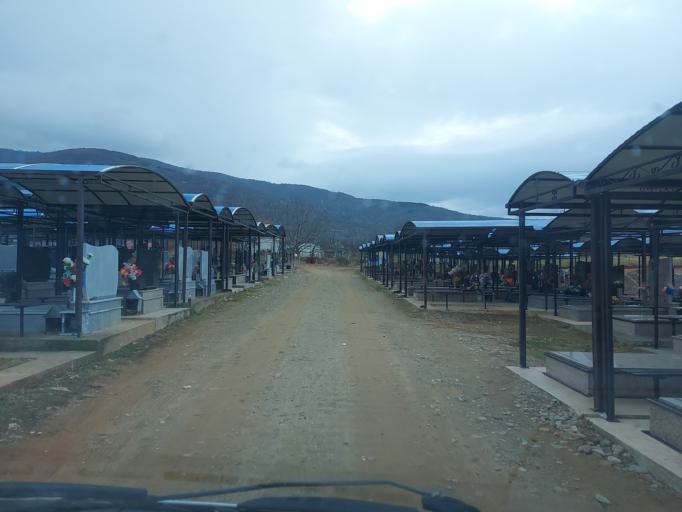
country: MK
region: Kriva Palanka
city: Kriva Palanka
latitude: 42.1865
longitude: 22.2939
